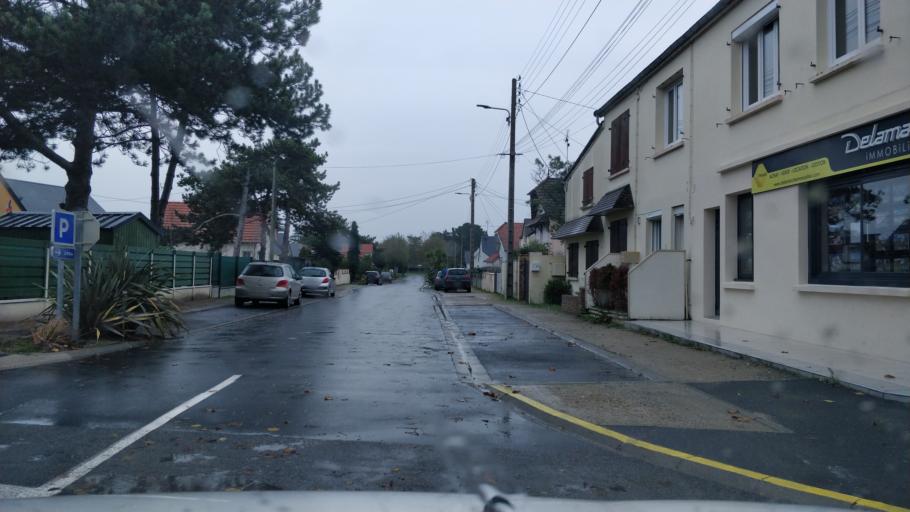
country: FR
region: Lower Normandy
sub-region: Departement de la Manche
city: Donville-les-Bains
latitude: 48.8963
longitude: -1.5677
